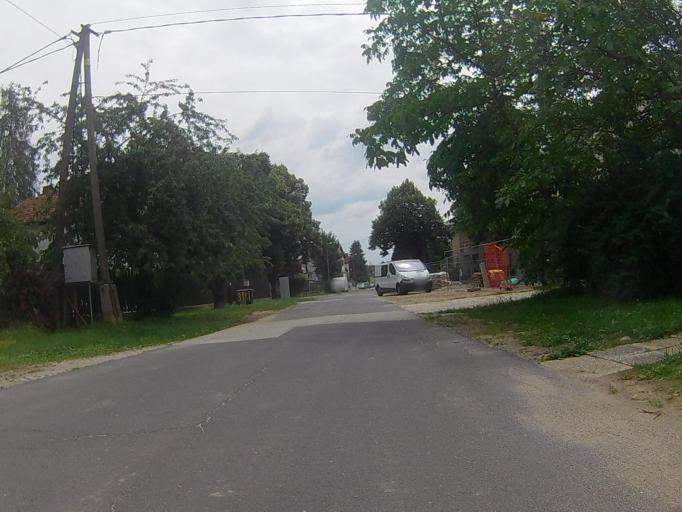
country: SI
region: Maribor
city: Maribor
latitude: 46.5649
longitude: 15.6314
